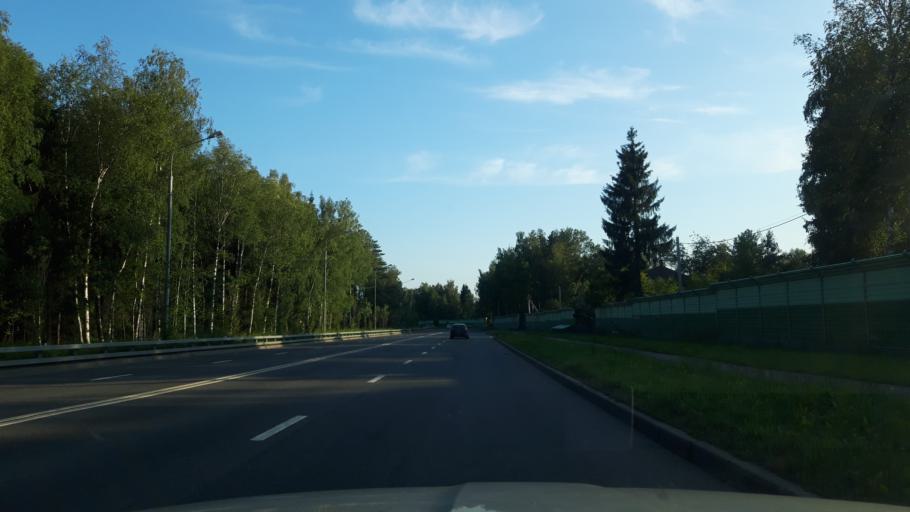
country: RU
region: Moskovskaya
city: Alabushevo
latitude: 56.0045
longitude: 37.1654
